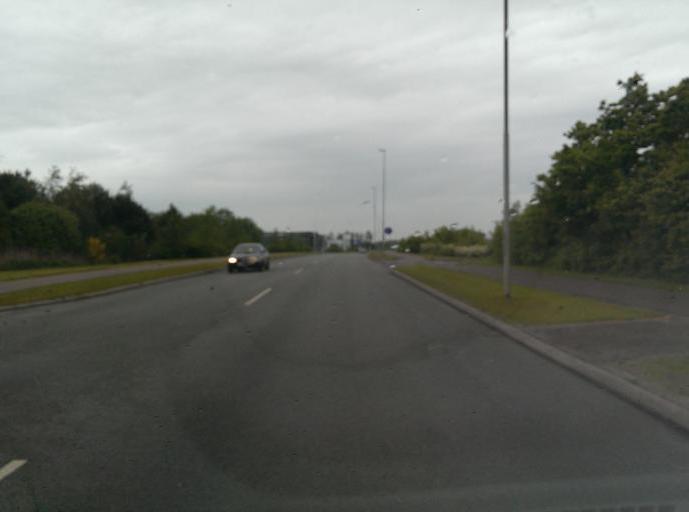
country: DK
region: South Denmark
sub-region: Esbjerg Kommune
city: Esbjerg
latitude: 55.5126
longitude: 8.4669
